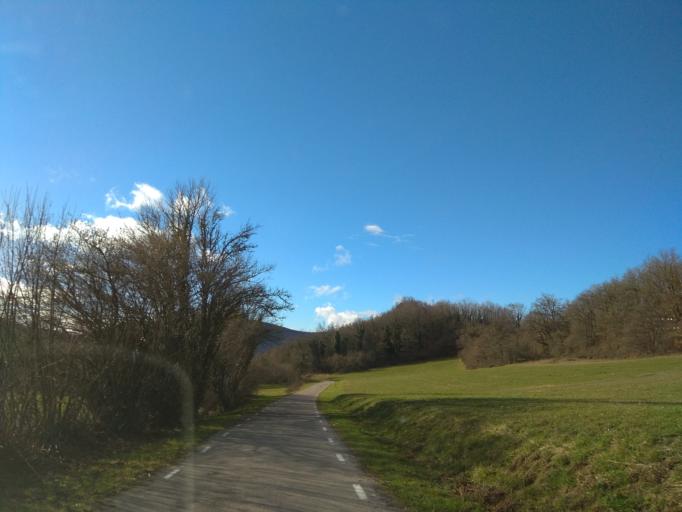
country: ES
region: Cantabria
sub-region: Provincia de Cantabria
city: San Martin de Elines
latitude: 42.9554
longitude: -3.8019
